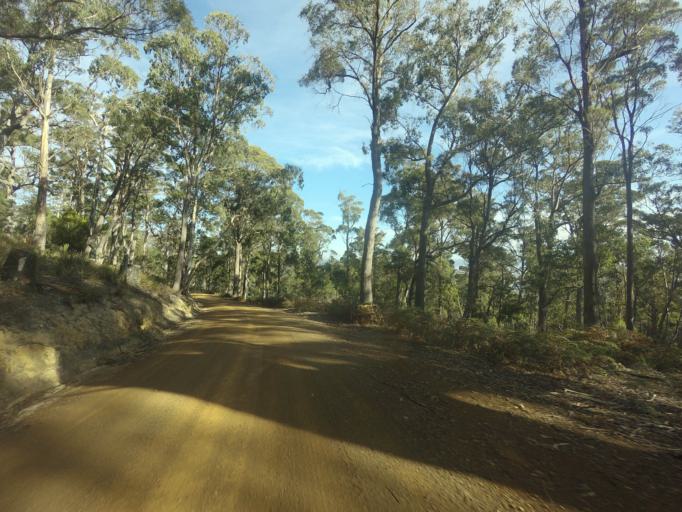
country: AU
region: Tasmania
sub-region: Sorell
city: Sorell
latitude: -42.5233
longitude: 147.4633
